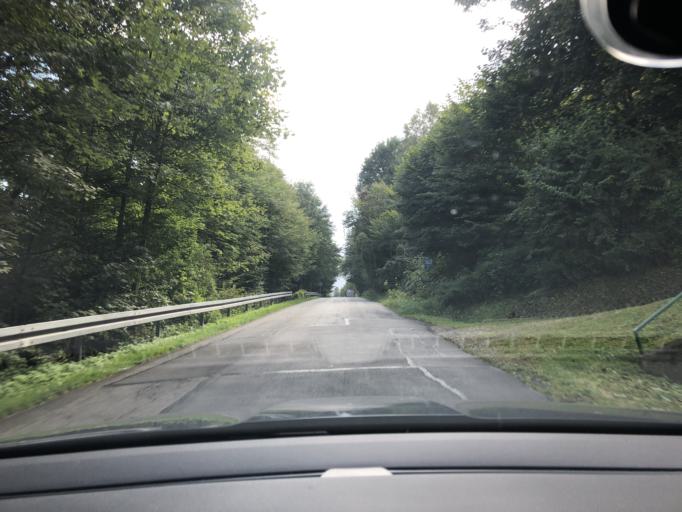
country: PL
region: Silesian Voivodeship
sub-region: Powiat zywiecki
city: Czernichow
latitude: 49.7429
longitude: 19.2051
